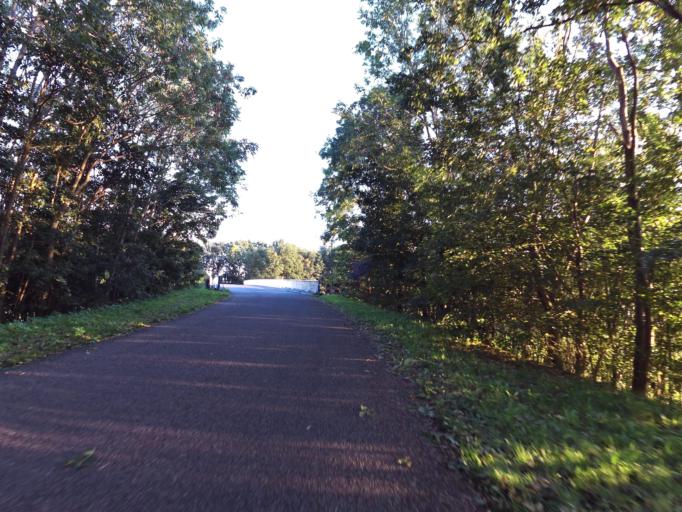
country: NL
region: Gelderland
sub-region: Gemeente Doesburg
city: Doesburg
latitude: 51.9293
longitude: 6.1612
